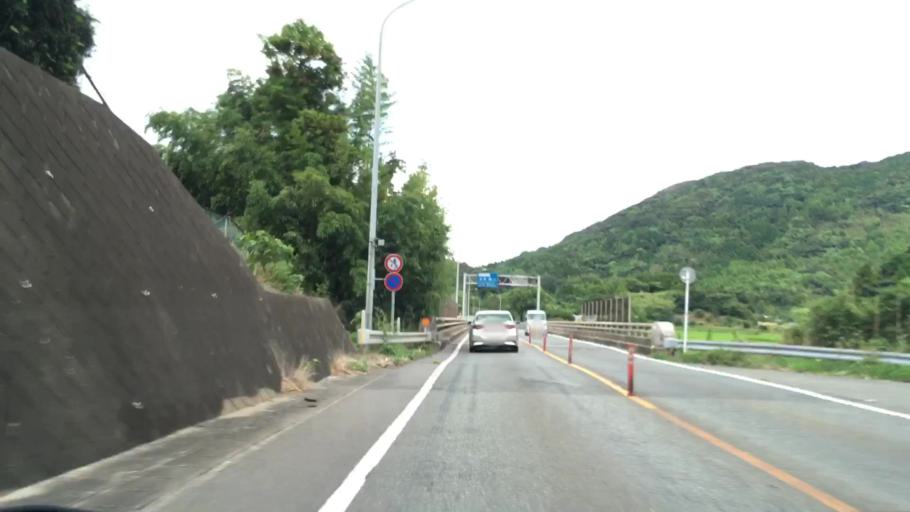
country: JP
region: Saga Prefecture
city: Karatsu
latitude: 33.4878
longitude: 130.0618
